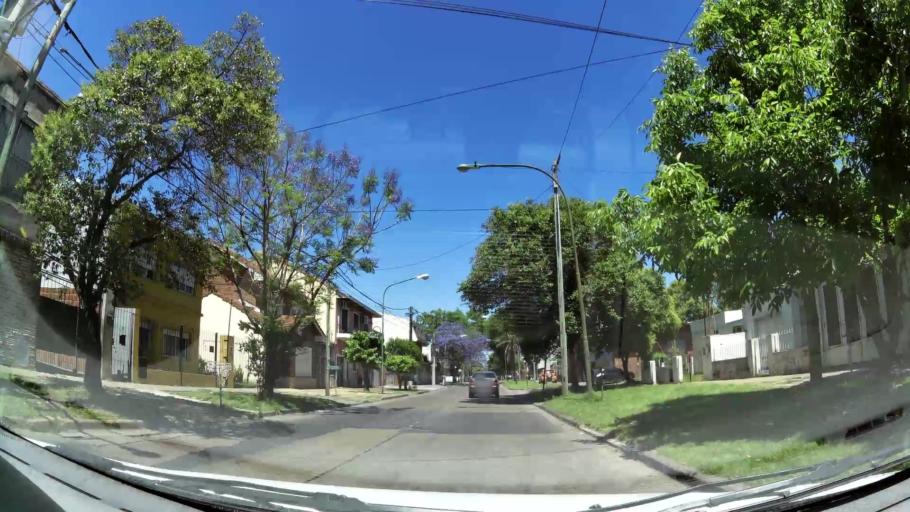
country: AR
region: Buenos Aires
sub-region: Partido de Vicente Lopez
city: Olivos
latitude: -34.5161
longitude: -58.5337
